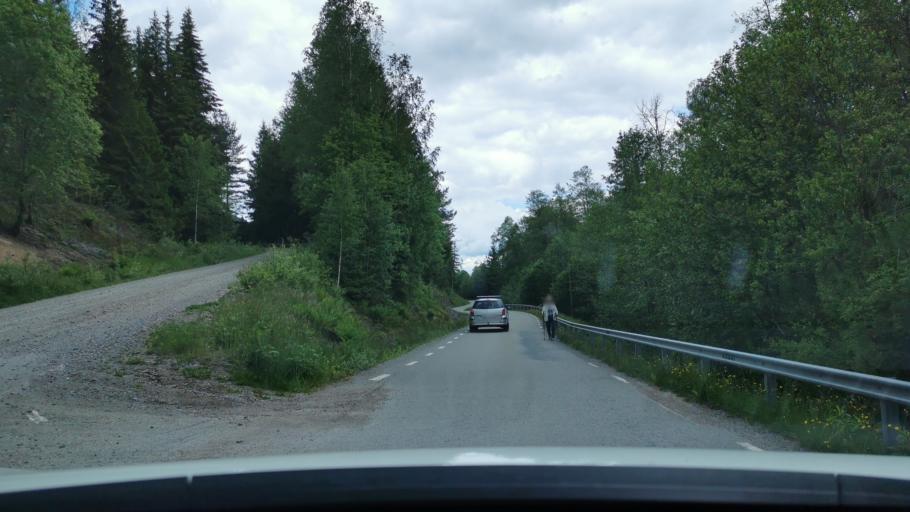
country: SE
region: Vaestra Goetaland
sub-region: Bengtsfors Kommun
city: Dals Langed
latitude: 58.8231
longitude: 12.3287
